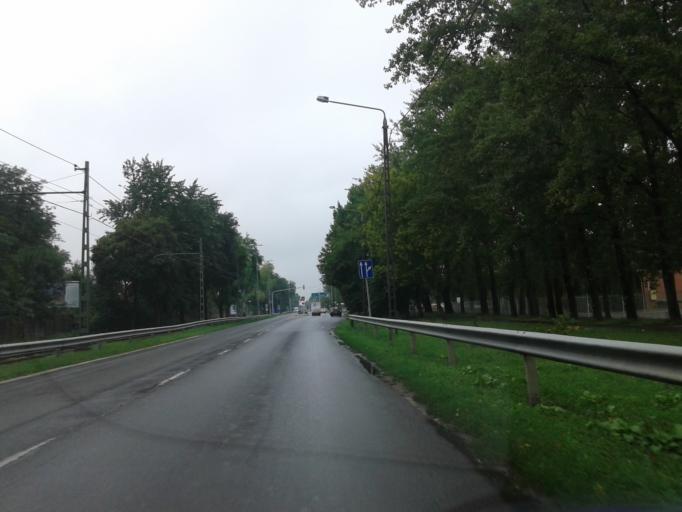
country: HU
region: Csongrad
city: Szeged
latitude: 46.2431
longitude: 20.1287
